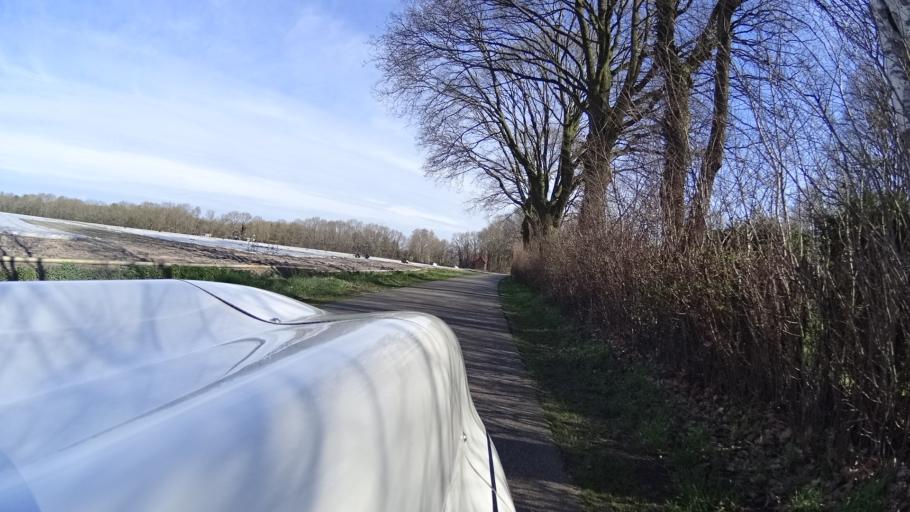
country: NL
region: North Brabant
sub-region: Gemeente Mill en Sint Hubert
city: Wilbertoord
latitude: 51.6998
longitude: 5.7630
